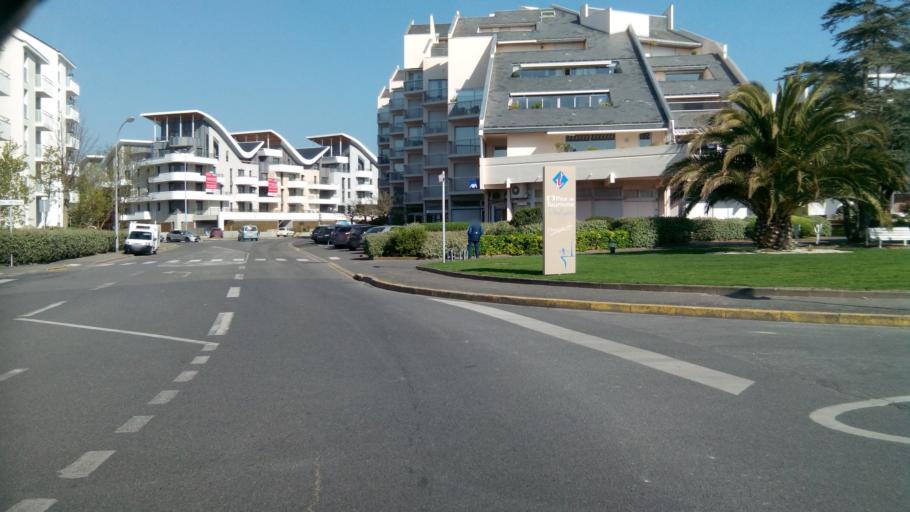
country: FR
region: Pays de la Loire
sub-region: Departement de la Loire-Atlantique
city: Le Pouliguen
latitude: 47.2803
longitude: -2.4280
